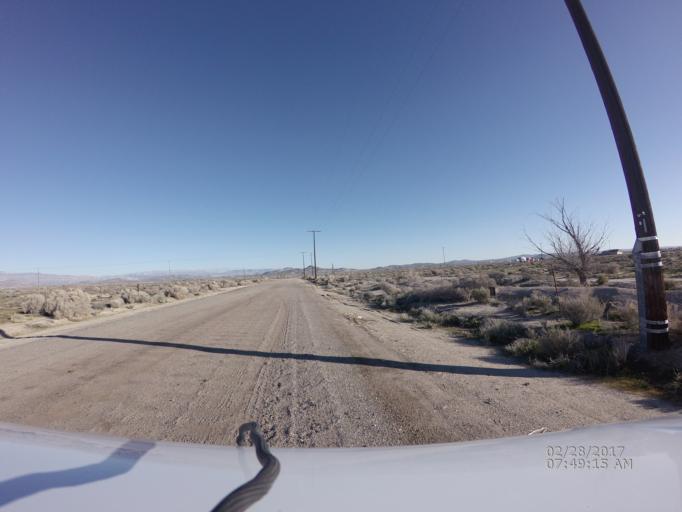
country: US
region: California
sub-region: Kern County
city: Rosamond
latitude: 34.8191
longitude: -118.1848
